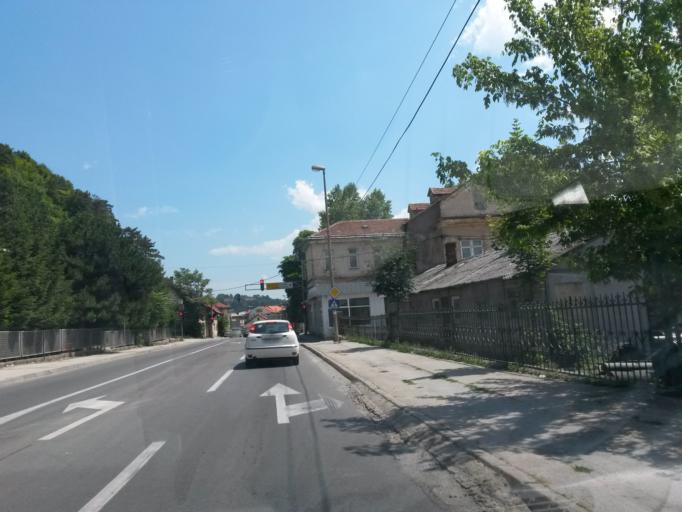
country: BA
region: Federation of Bosnia and Herzegovina
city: Travnik
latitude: 44.2283
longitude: 17.6560
